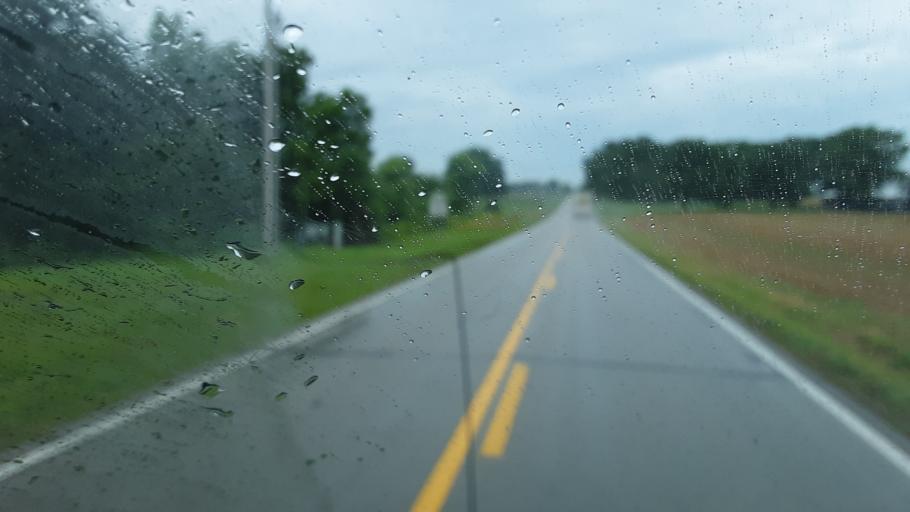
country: US
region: Kentucky
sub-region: Logan County
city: Russellville
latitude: 36.8041
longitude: -86.9562
